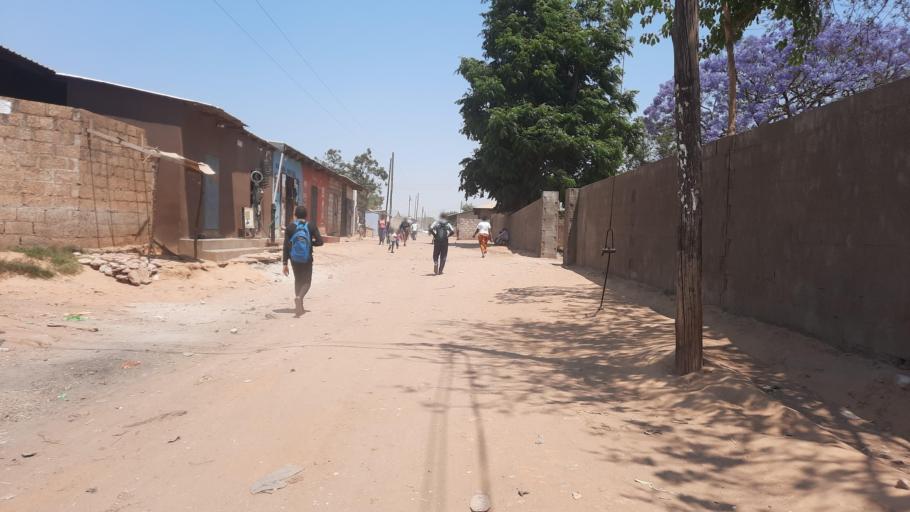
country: ZM
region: Lusaka
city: Lusaka
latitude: -15.4039
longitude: 28.3741
